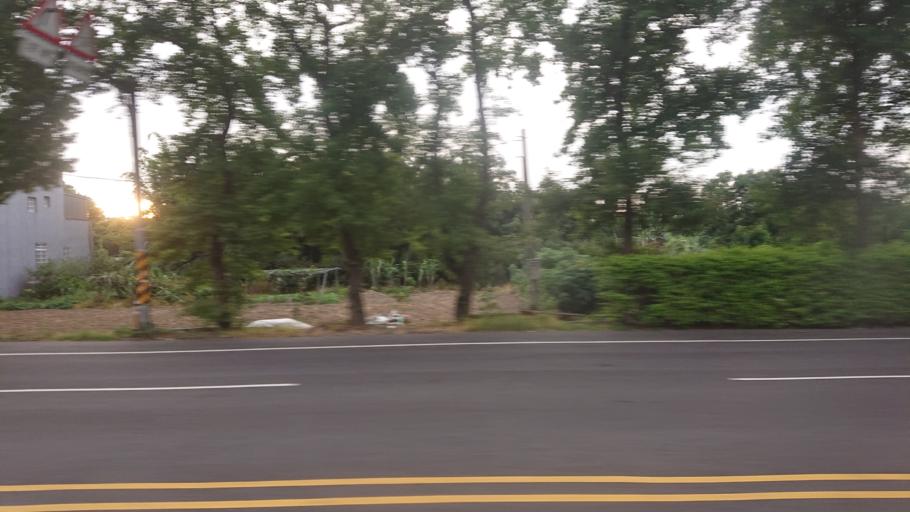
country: TW
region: Taiwan
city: Daxi
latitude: 24.8770
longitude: 121.2540
